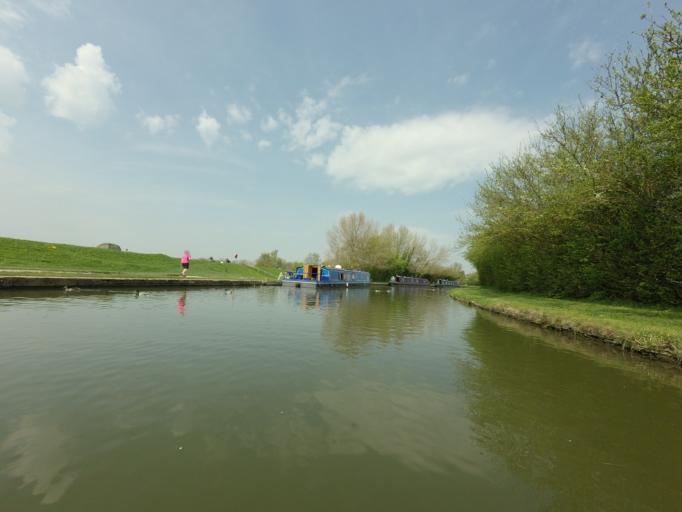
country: GB
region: England
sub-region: Hertfordshire
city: Tring
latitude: 51.8167
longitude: -0.6666
